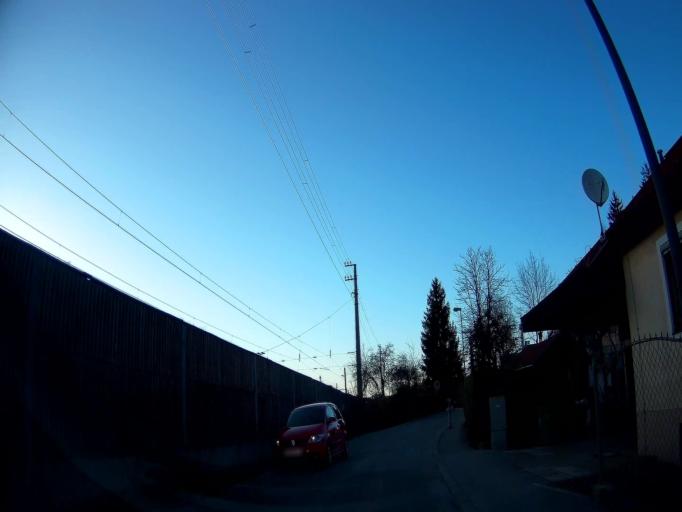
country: BJ
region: Borgou
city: Parakou
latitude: 9.5610
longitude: 2.6141
